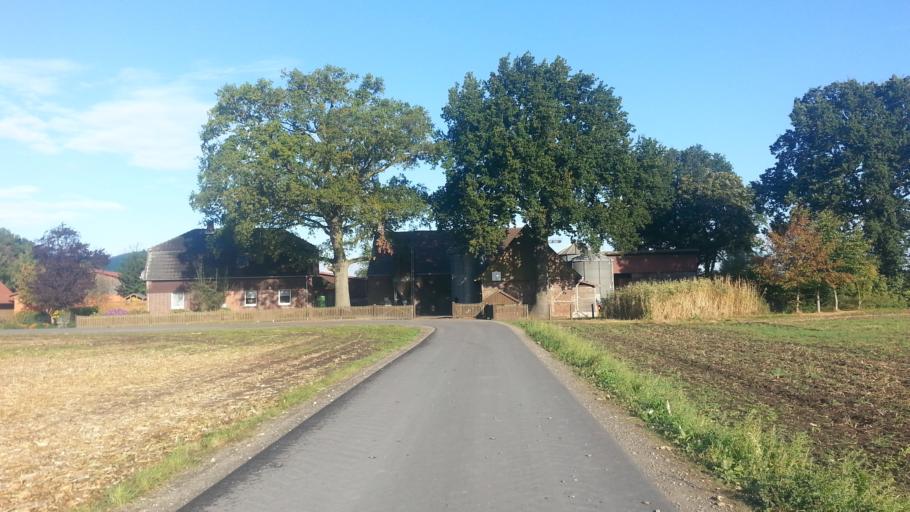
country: DE
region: North Rhine-Westphalia
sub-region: Regierungsbezirk Munster
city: Muenster
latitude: 51.9546
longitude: 7.5808
